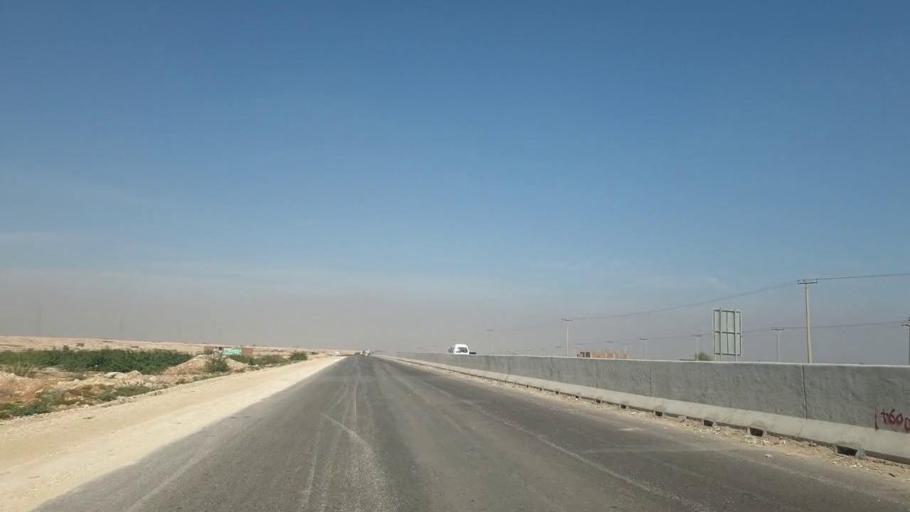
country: PK
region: Sindh
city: Jamshoro
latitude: 25.4874
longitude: 68.2720
